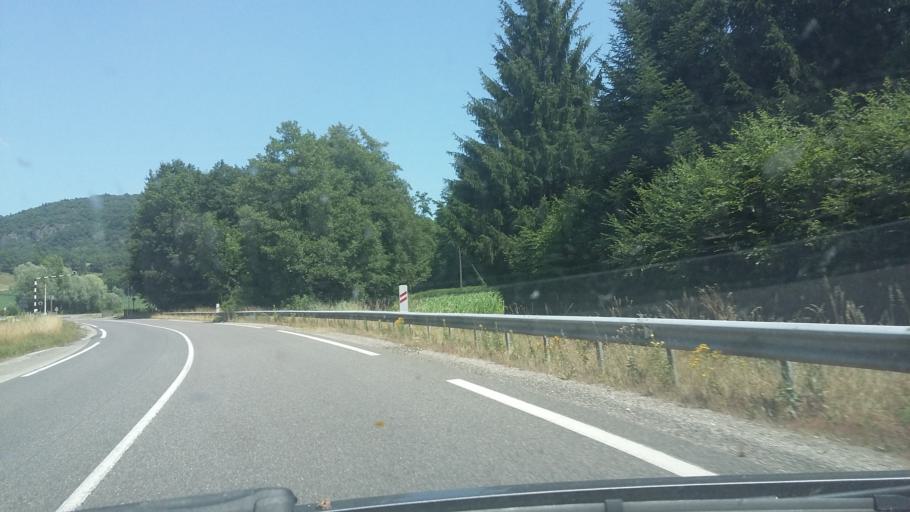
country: FR
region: Rhone-Alpes
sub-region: Departement de l'Ain
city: Belley
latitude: 45.7754
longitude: 5.6977
